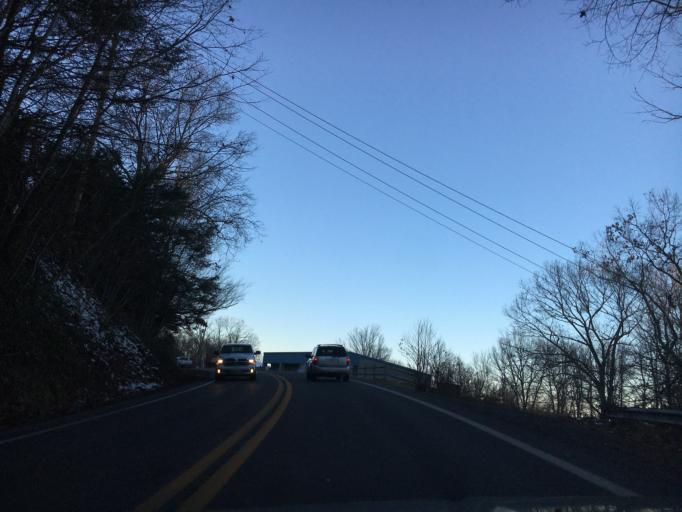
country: US
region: West Virginia
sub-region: Raleigh County
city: Beaver
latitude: 37.7658
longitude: -81.1567
